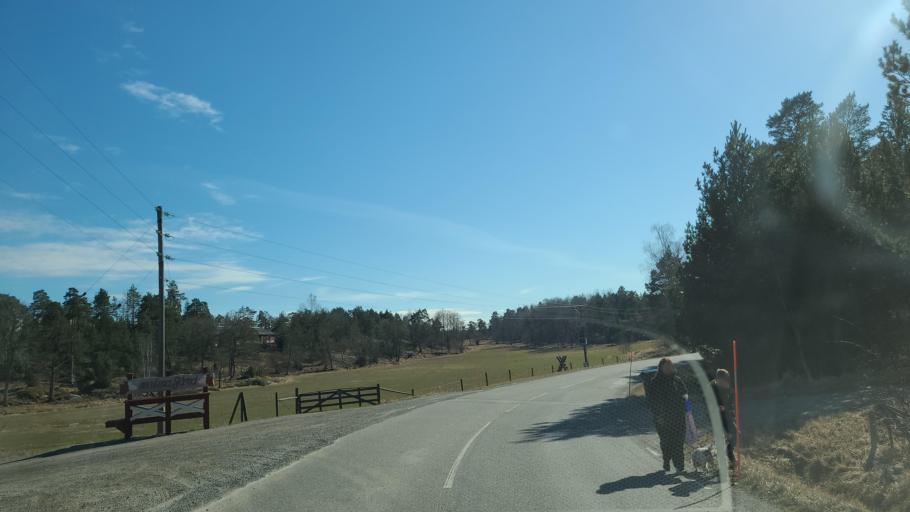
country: SE
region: Stockholm
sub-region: Varmdo Kommun
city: Holo
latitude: 59.2803
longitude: 18.6113
